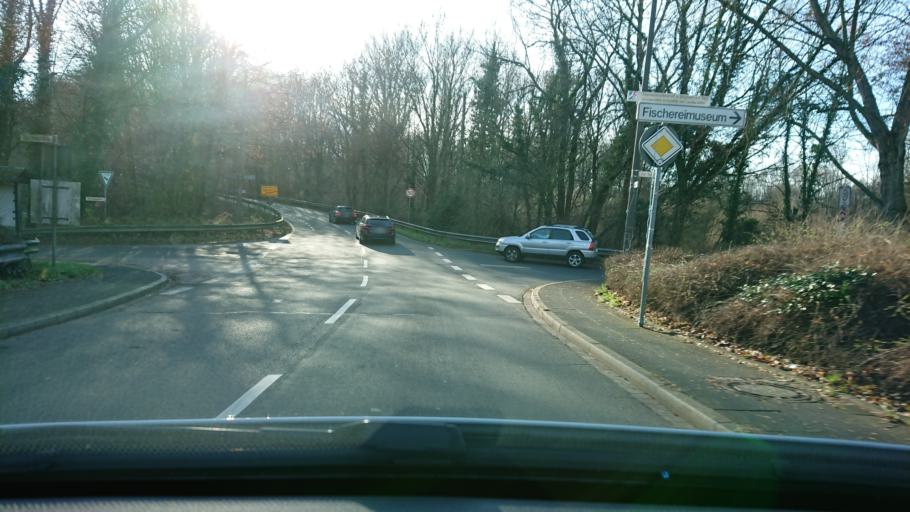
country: DE
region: North Rhine-Westphalia
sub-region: Regierungsbezirk Koln
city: Bonn
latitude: 50.7722
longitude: 7.0965
